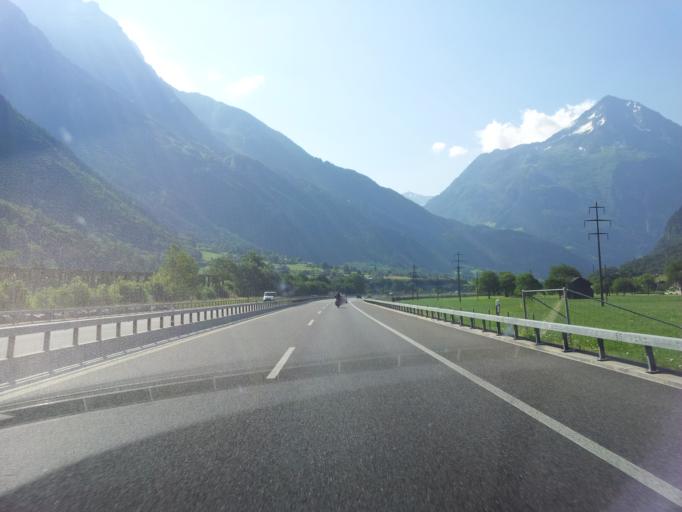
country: CH
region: Uri
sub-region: Uri
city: Erstfeld
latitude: 46.8119
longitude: 8.6572
